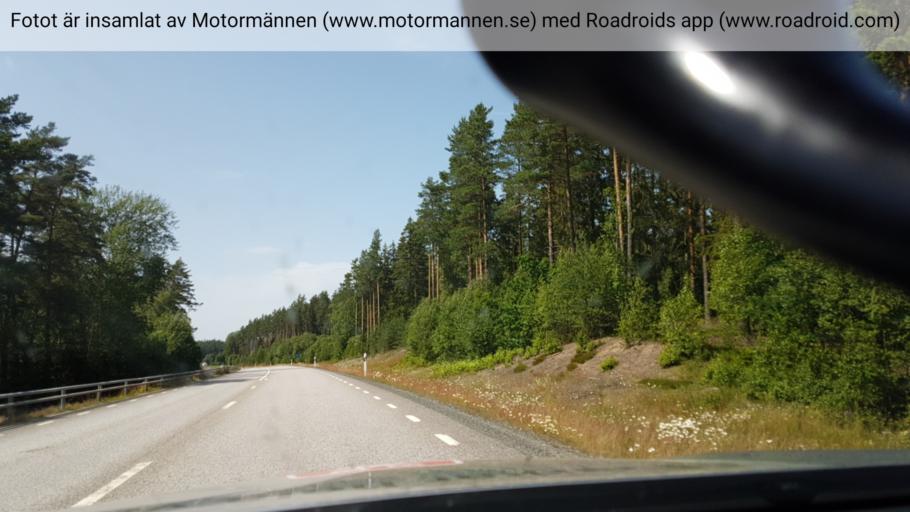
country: SE
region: Joenkoeping
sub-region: Aneby Kommun
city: Aneby
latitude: 57.7664
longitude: 14.9042
